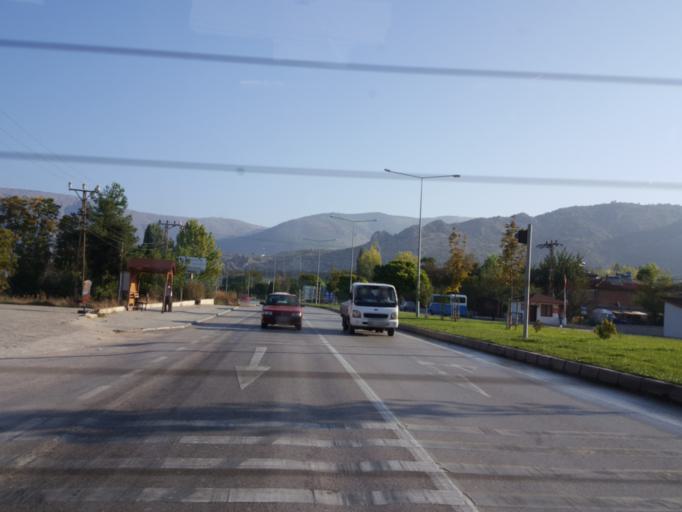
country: TR
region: Amasya
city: Amasya
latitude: 40.6013
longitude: 35.8096
